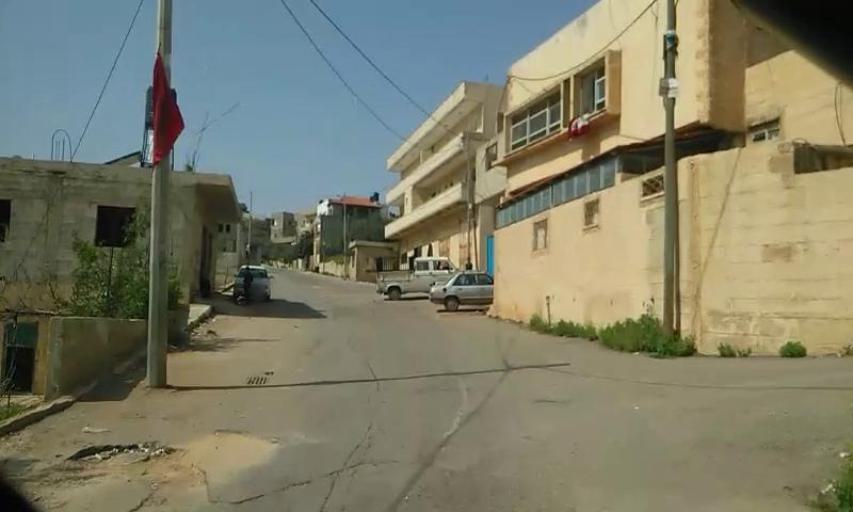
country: PS
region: West Bank
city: `Anin
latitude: 32.5004
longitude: 35.1724
